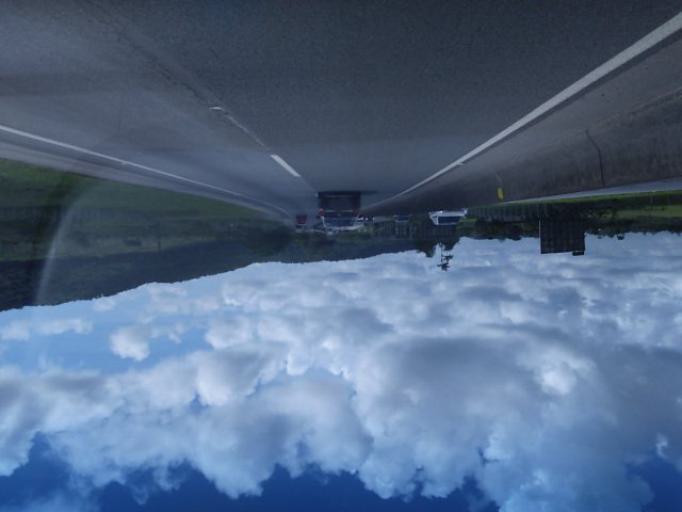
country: BR
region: Santa Catarina
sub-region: Barra Velha
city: Barra Velha
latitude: -26.5721
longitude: -48.7223
